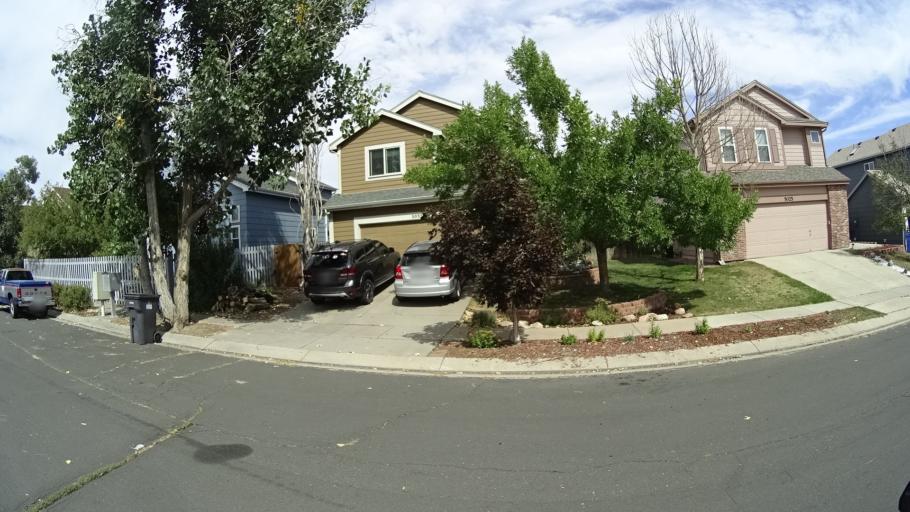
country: US
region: Colorado
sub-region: El Paso County
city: Cimarron Hills
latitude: 38.9057
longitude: -104.7091
